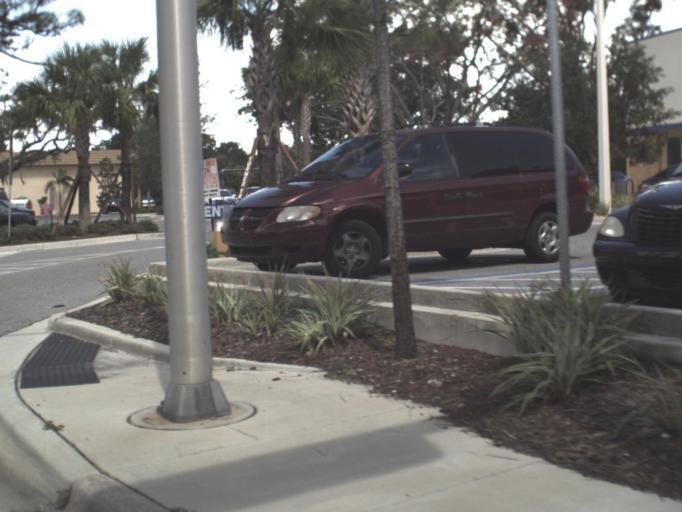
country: US
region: Florida
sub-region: Manatee County
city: Whitfield
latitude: 27.3790
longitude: -82.5557
